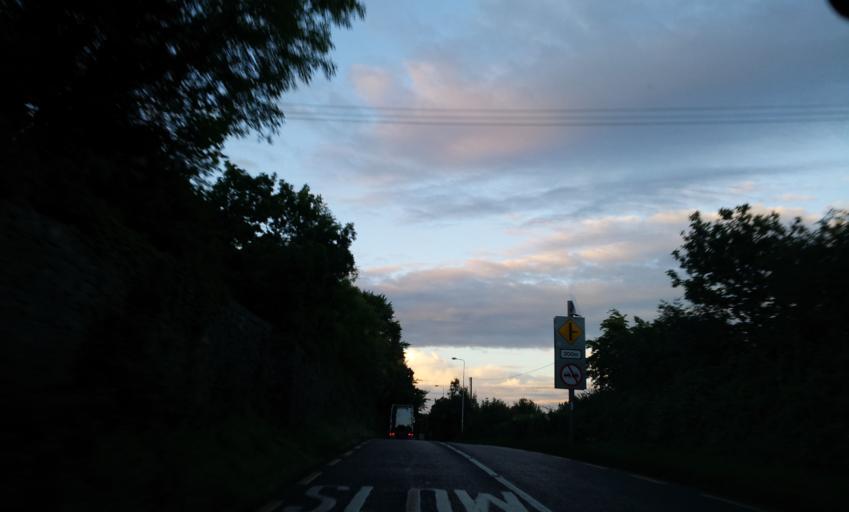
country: IE
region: Munster
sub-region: County Limerick
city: Adare
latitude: 52.5535
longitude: -8.8069
